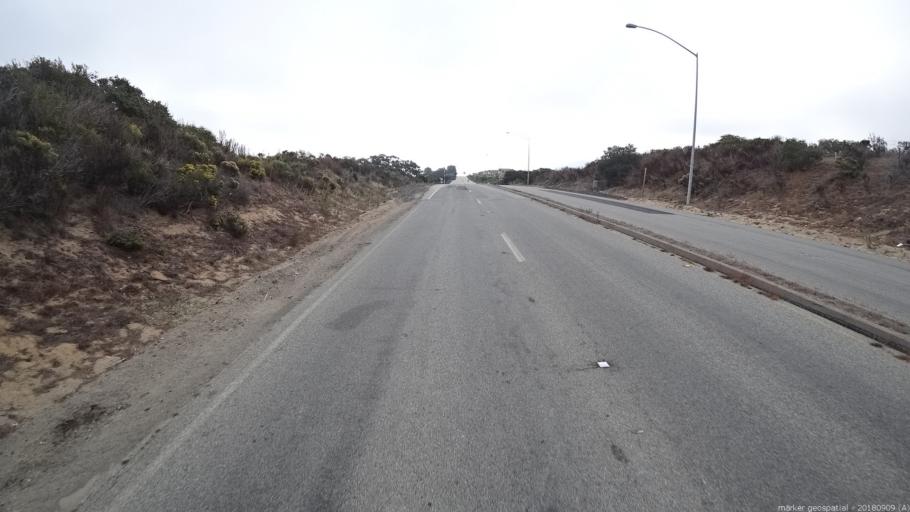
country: US
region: California
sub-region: Monterey County
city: Marina
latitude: 36.6607
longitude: -121.7434
